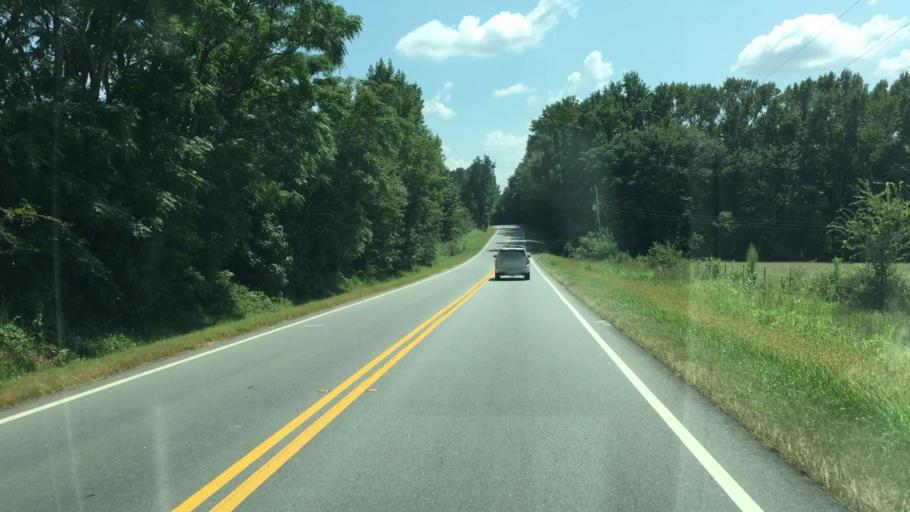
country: US
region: Georgia
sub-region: Oconee County
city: Watkinsville
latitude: 33.7942
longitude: -83.4251
